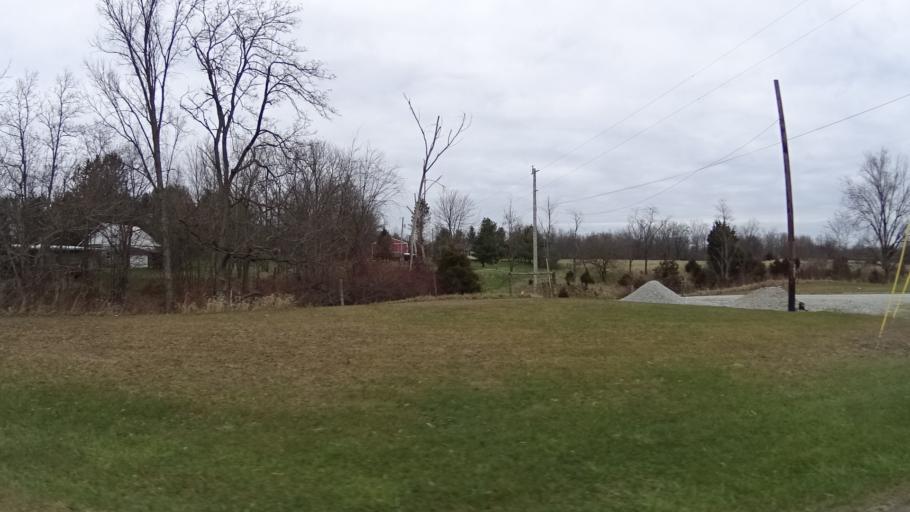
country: US
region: Ohio
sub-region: Lorain County
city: Wellington
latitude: 41.1692
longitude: -82.2511
